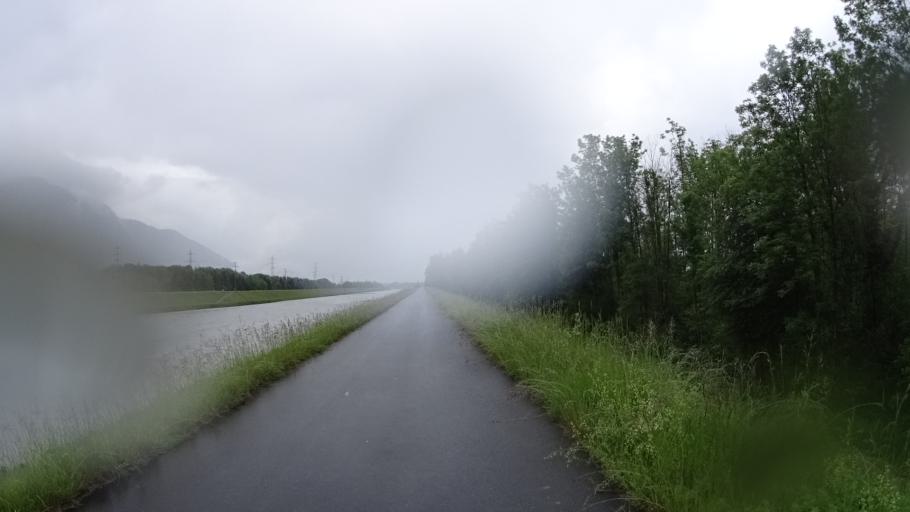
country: LI
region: Gamprin
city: Gamprin
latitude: 47.2258
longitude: 9.5063
